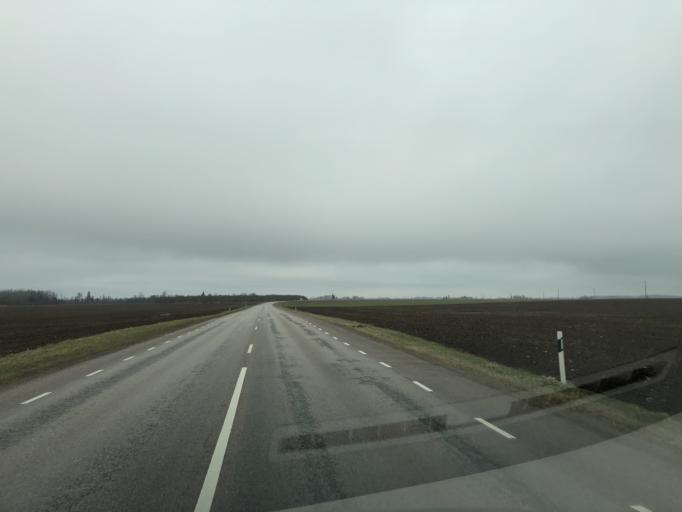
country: EE
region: Laeaene-Virumaa
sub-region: Vaeike-Maarja vald
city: Vaike-Maarja
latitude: 59.1848
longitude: 26.2660
